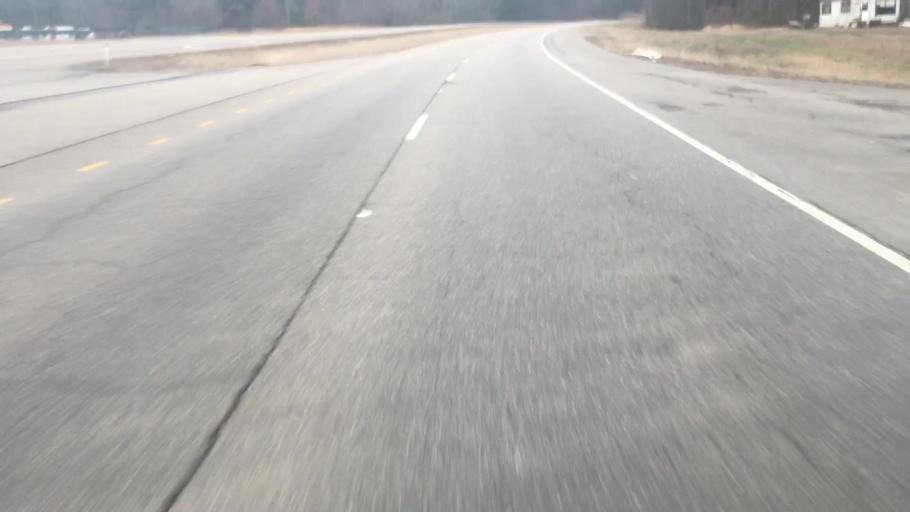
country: US
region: Alabama
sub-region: Walker County
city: Sumiton
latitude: 33.7742
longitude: -87.0754
